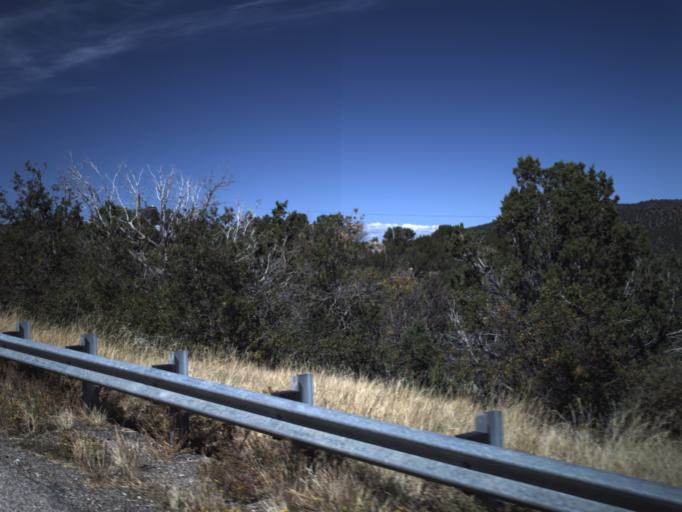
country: US
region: Utah
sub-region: Washington County
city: Enterprise
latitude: 37.5199
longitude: -113.6378
